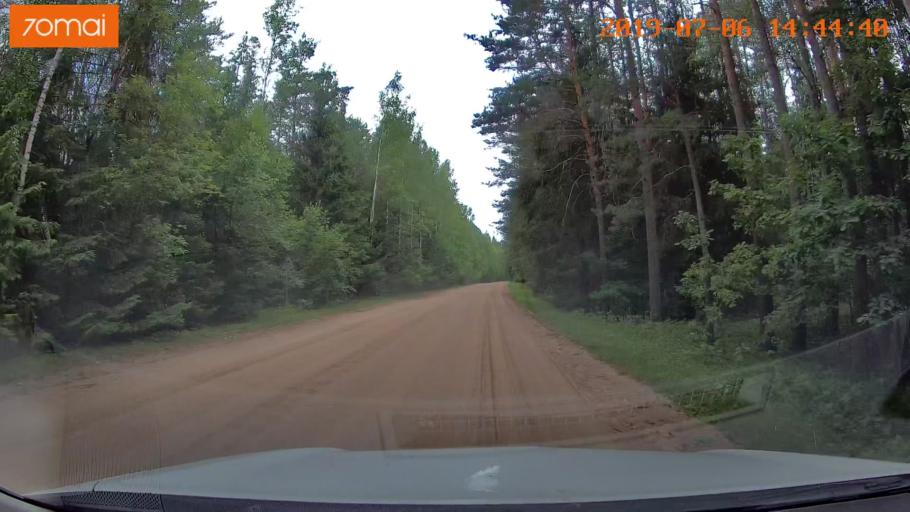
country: BY
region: Minsk
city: Ivyanyets
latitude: 53.9642
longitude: 26.6923
